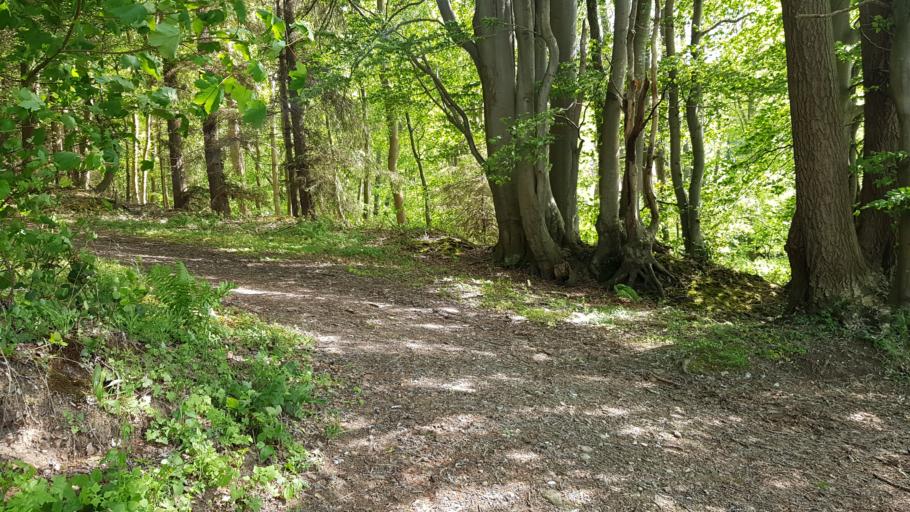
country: DE
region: Schleswig-Holstein
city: Rieseby
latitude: 54.5710
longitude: 9.8073
